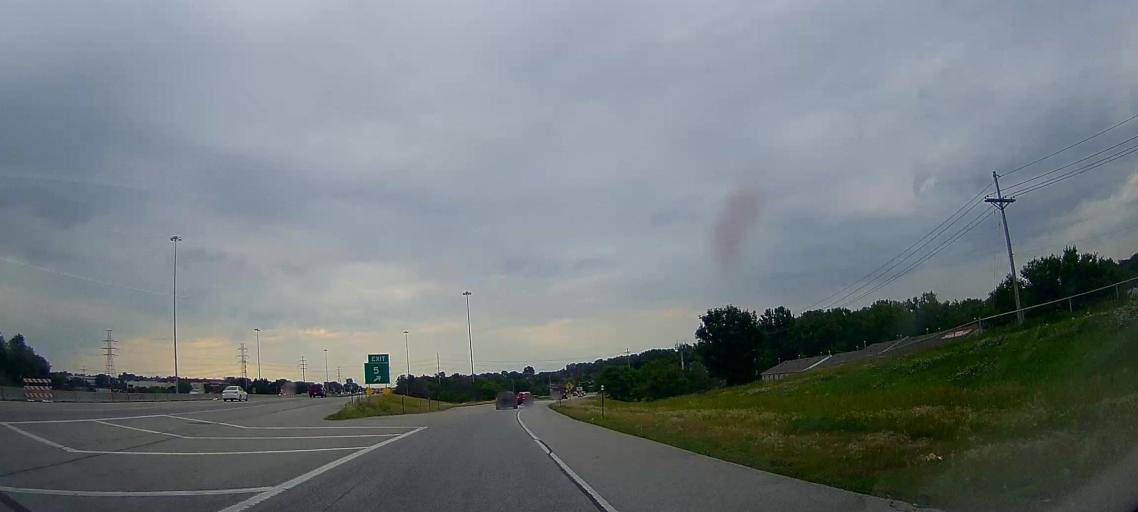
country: US
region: Nebraska
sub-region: Douglas County
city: Ralston
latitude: 41.3040
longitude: -96.0706
